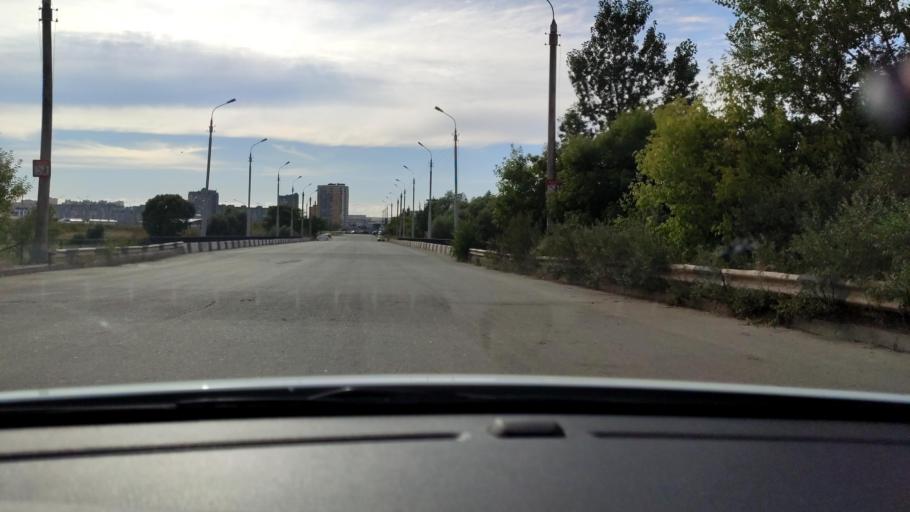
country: RU
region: Tatarstan
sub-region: Gorod Kazan'
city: Kazan
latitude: 55.8238
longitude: 49.1693
